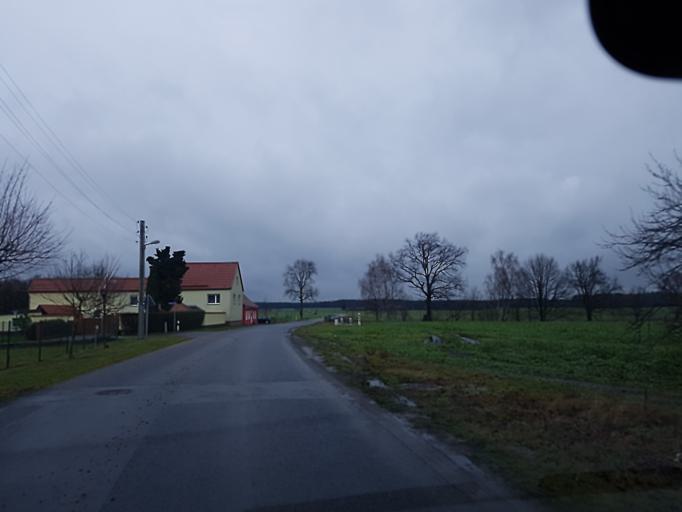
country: DE
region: Brandenburg
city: Finsterwalde
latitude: 51.6060
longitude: 13.6690
